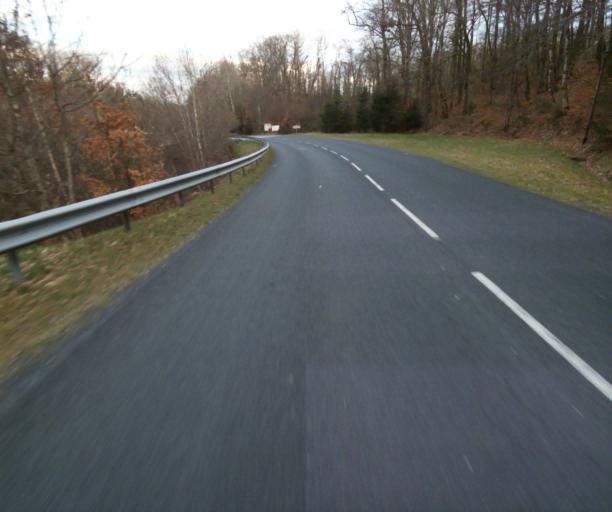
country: FR
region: Limousin
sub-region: Departement de la Correze
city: Correze
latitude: 45.2800
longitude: 1.9603
